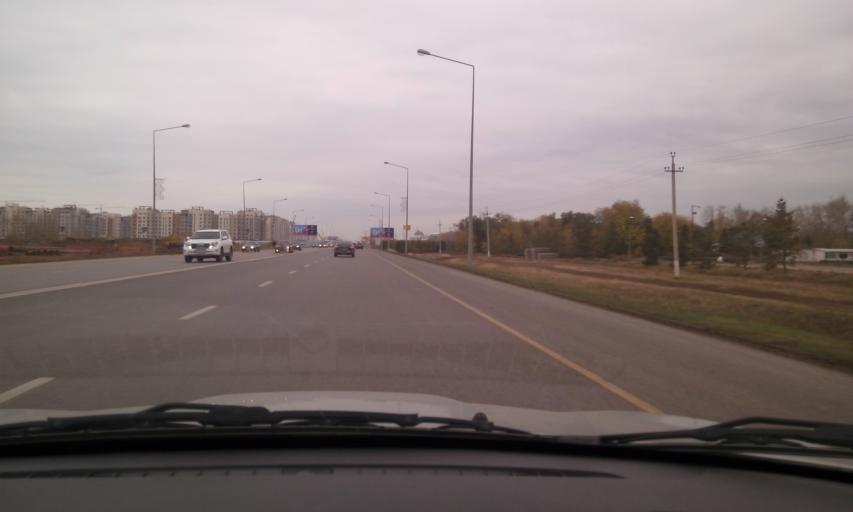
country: KZ
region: Astana Qalasy
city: Astana
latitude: 51.1037
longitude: 71.4076
